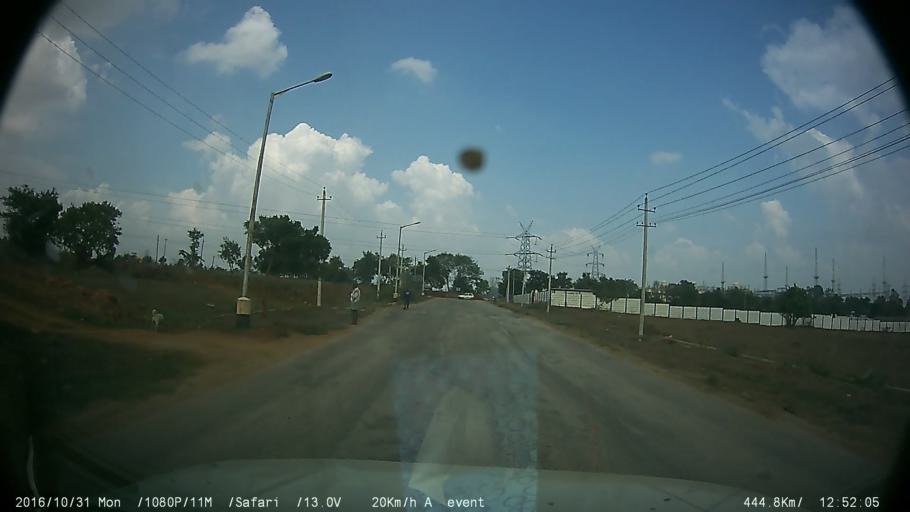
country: IN
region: Karnataka
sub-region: Mysore
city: Mysore
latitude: 12.3664
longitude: 76.5620
